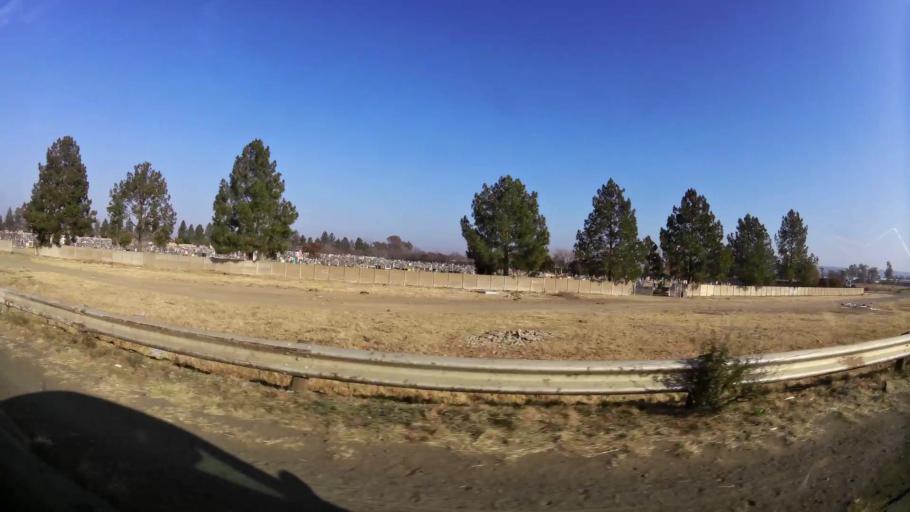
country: ZA
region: Orange Free State
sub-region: Mangaung Metropolitan Municipality
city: Bloemfontein
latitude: -29.1376
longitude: 26.2669
